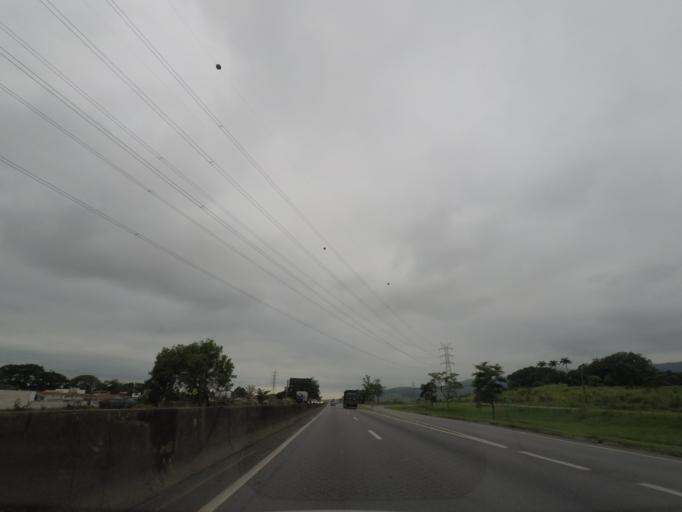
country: BR
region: Sao Paulo
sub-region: Aparecida
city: Aparecida
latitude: -22.9033
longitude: -45.3079
